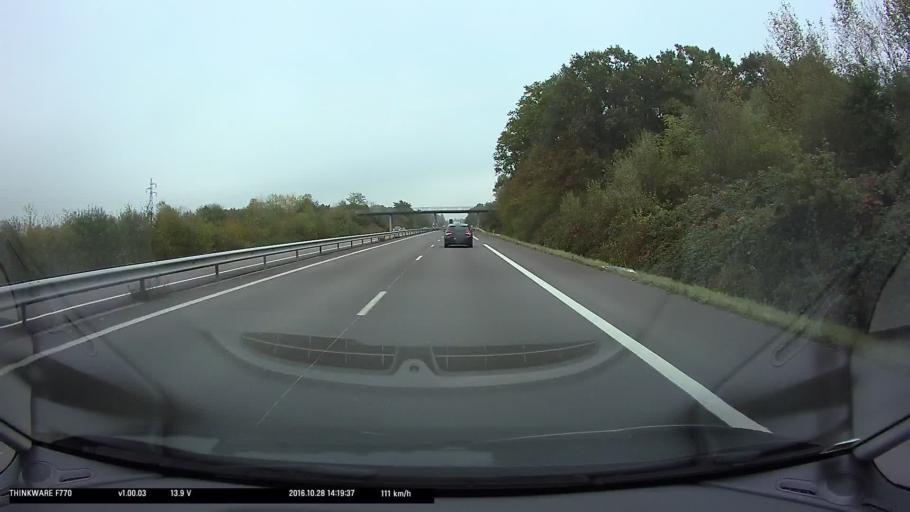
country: FR
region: Lorraine
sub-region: Departement de Meurthe-et-Moselle
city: Chanteheux
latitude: 48.5821
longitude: 6.5931
